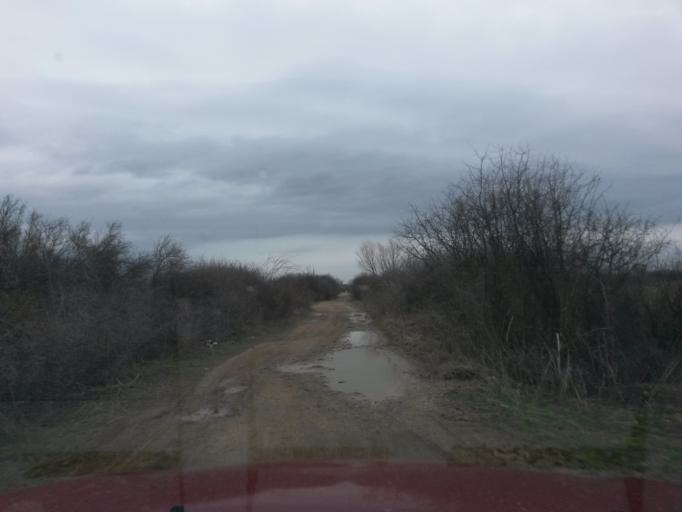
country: SK
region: Kosicky
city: Michalovce
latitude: 48.6957
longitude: 21.9044
